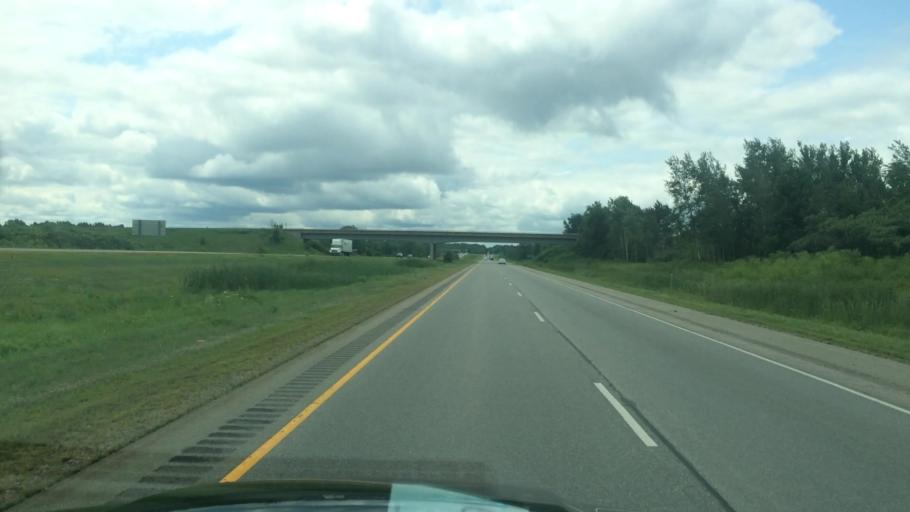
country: US
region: Wisconsin
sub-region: Marathon County
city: Mosinee
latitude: 44.7452
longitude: -89.6801
